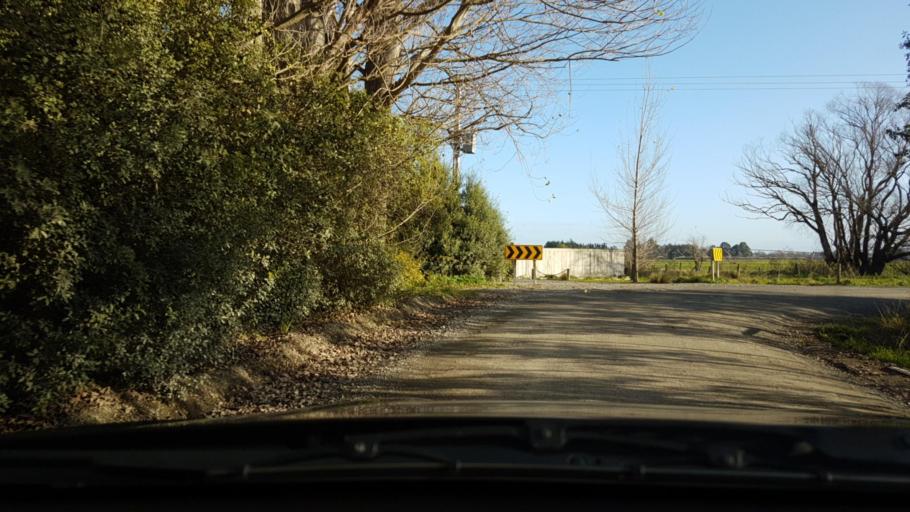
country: NZ
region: Canterbury
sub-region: Waimakariri District
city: Woodend
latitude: -43.3230
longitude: 172.6312
